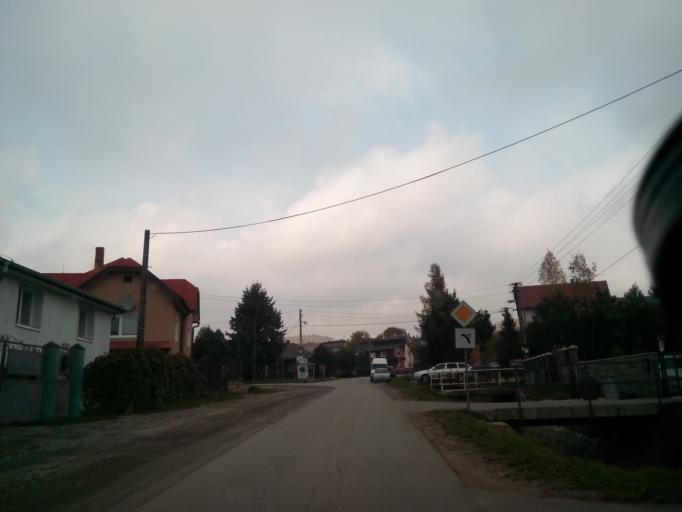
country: SK
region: Kosicky
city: Kosice
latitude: 48.7271
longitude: 21.1424
